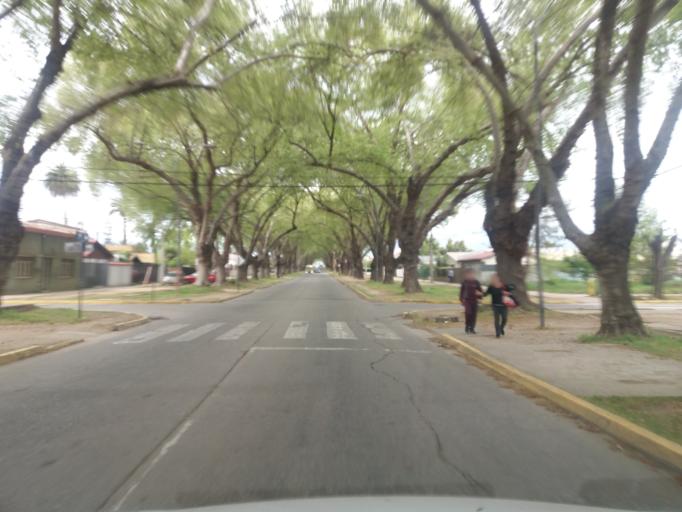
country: CL
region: Valparaiso
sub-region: Provincia de Marga Marga
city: Limache
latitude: -32.9881
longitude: -71.2693
